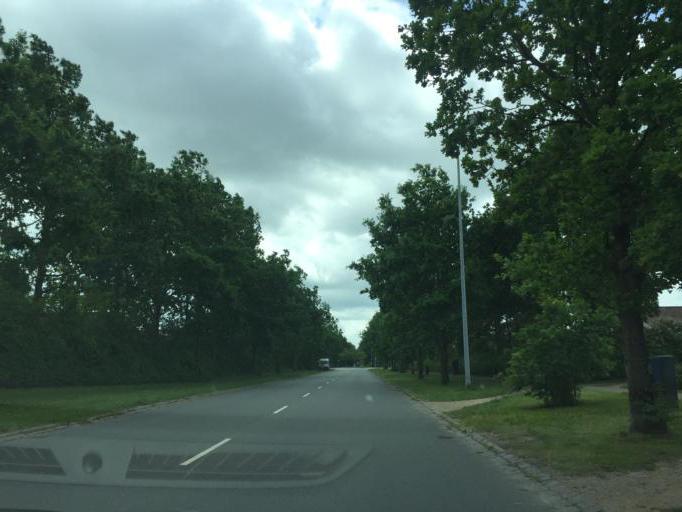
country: DK
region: South Denmark
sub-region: Odense Kommune
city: Neder Holluf
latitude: 55.3634
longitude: 10.4501
